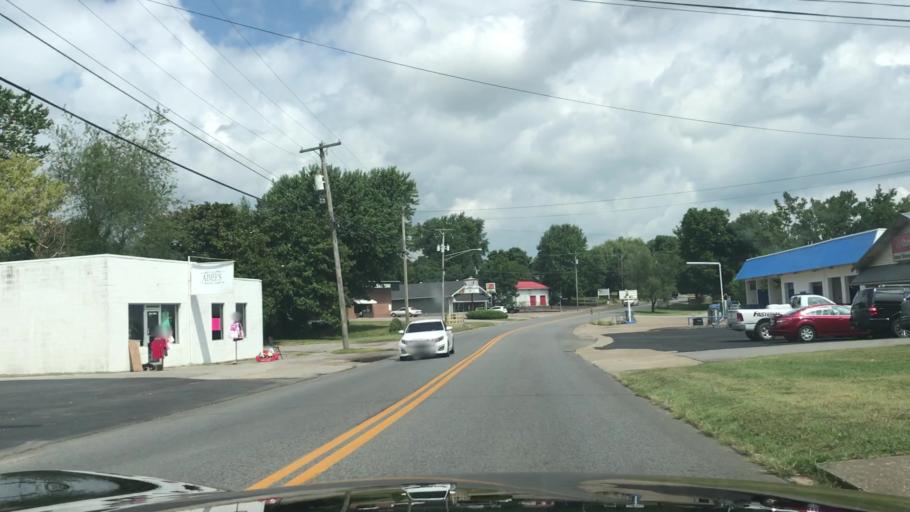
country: US
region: Kentucky
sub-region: Muhlenberg County
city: Greenville
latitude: 37.2087
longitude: -87.1802
